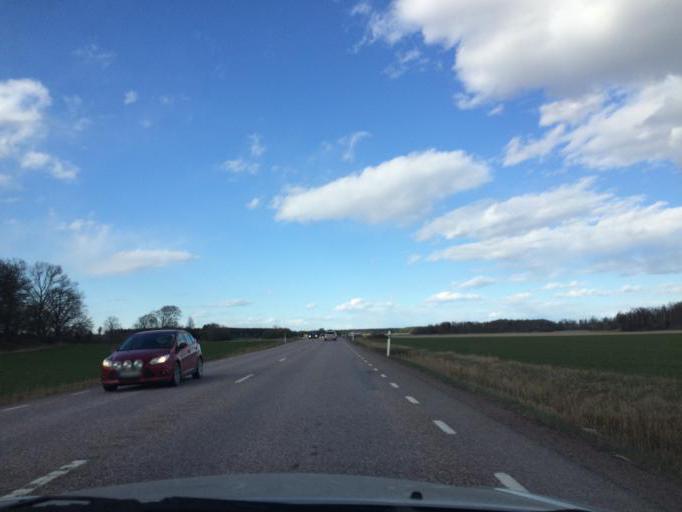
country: SE
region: Vaestmanland
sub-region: Hallstahammars Kommun
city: Kolback
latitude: 59.5378
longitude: 16.3234
